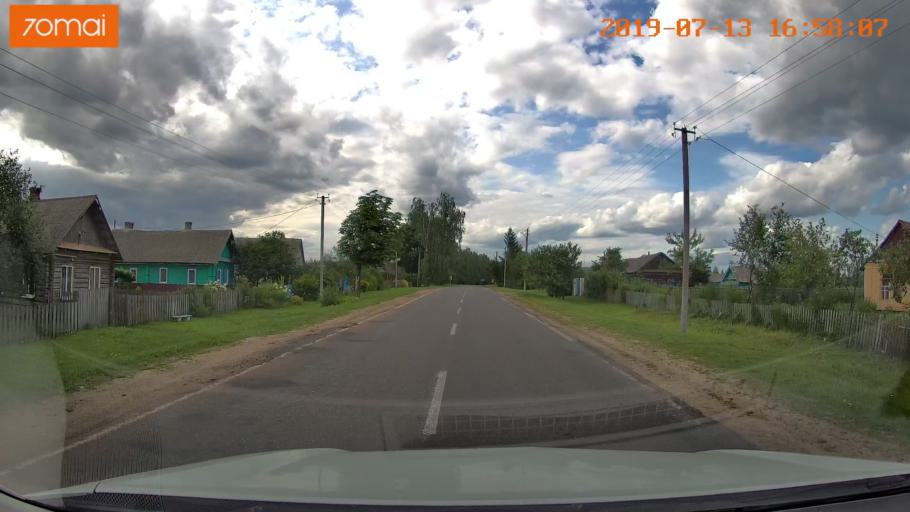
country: BY
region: Mogilev
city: Kirawsk
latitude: 53.2855
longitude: 29.4450
